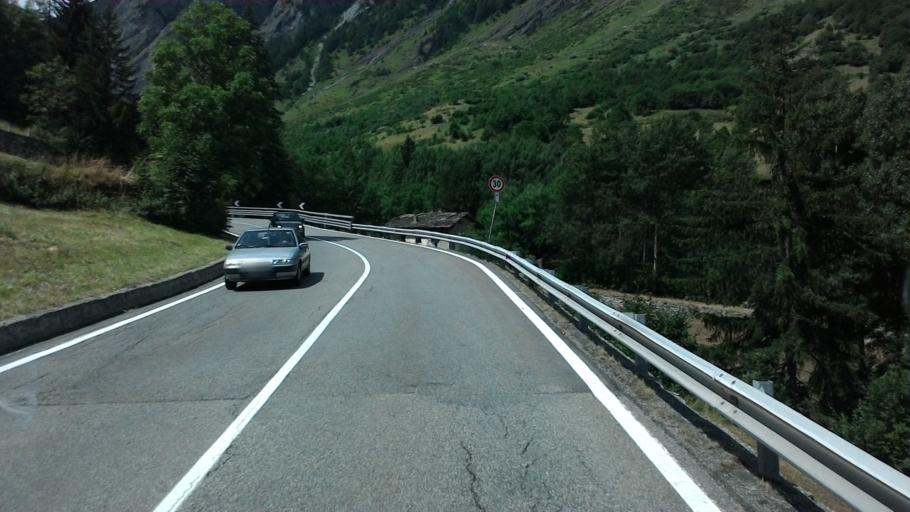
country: IT
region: Aosta Valley
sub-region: Valle d'Aosta
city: La Thuile
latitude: 45.7292
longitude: 6.9569
